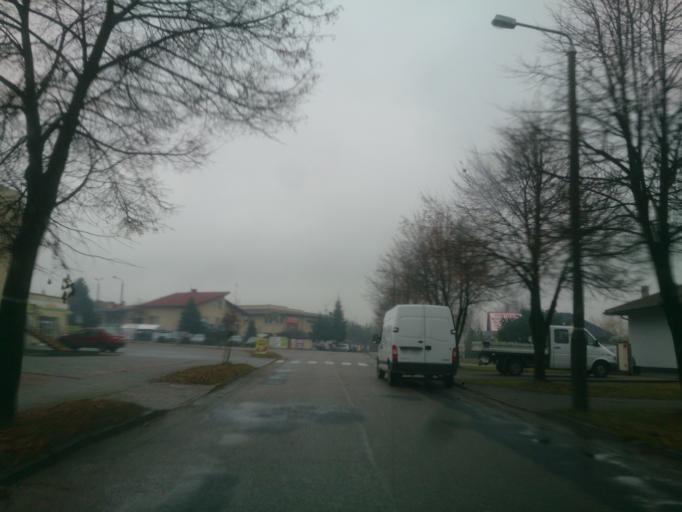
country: PL
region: Kujawsko-Pomorskie
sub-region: Powiat brodnicki
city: Brodnica
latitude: 53.2620
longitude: 19.3868
